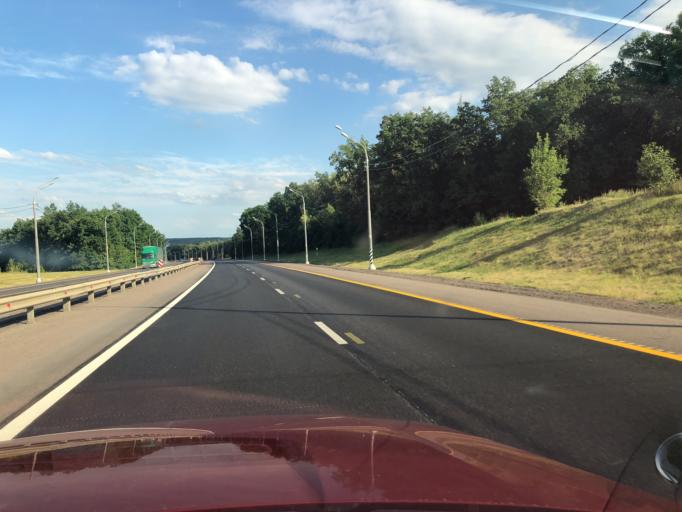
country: RU
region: Lipetsk
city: Zadonsk
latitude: 52.3857
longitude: 38.8691
